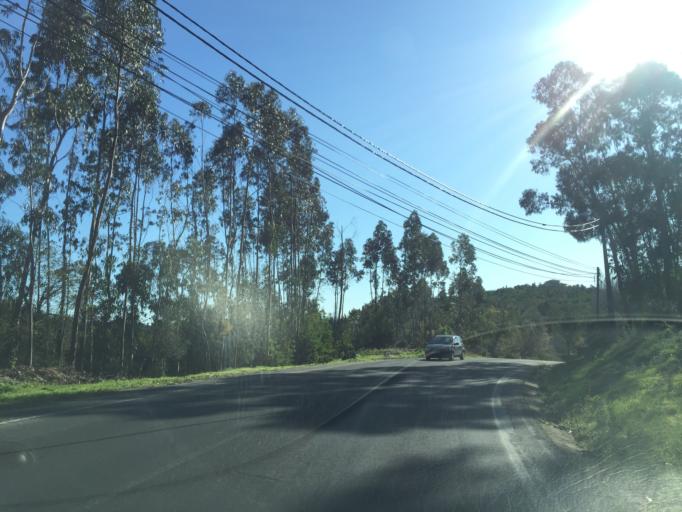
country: PT
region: Lisbon
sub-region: Sintra
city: Belas
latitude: 38.7984
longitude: -9.2698
